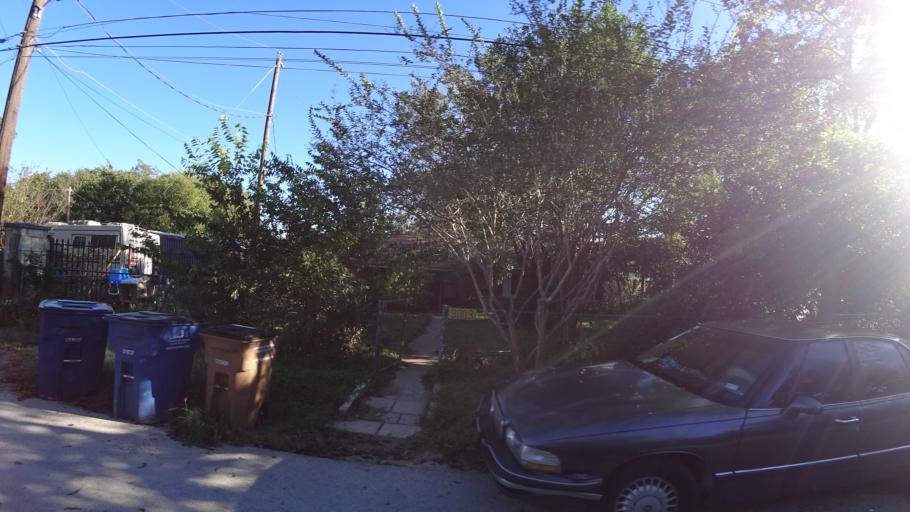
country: US
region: Texas
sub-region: Travis County
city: Hornsby Bend
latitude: 30.2069
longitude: -97.6403
